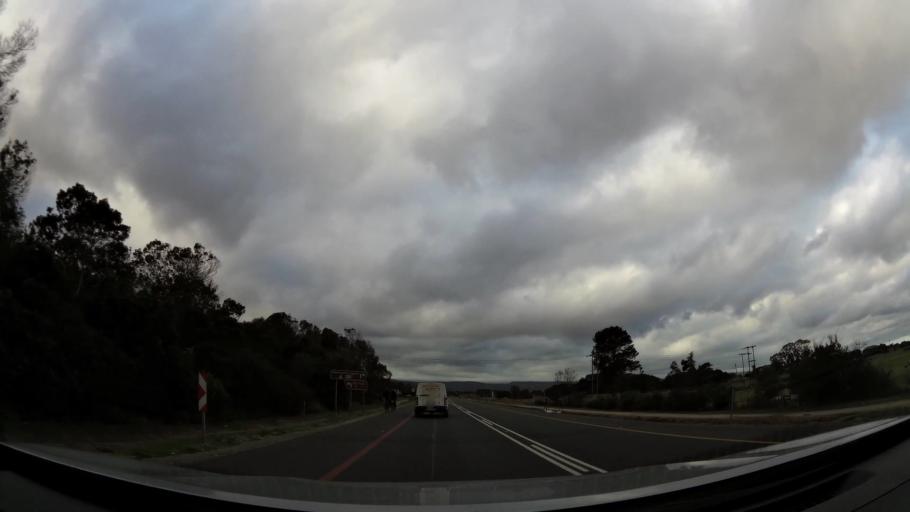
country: ZA
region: Western Cape
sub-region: Eden District Municipality
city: Plettenberg Bay
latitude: -34.0377
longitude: 23.3714
